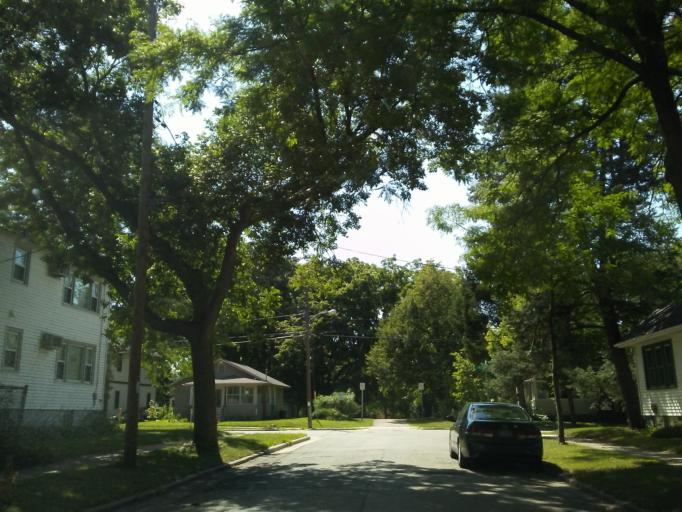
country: US
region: Wisconsin
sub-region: Dane County
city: Monona
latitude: 43.1014
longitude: -89.3410
